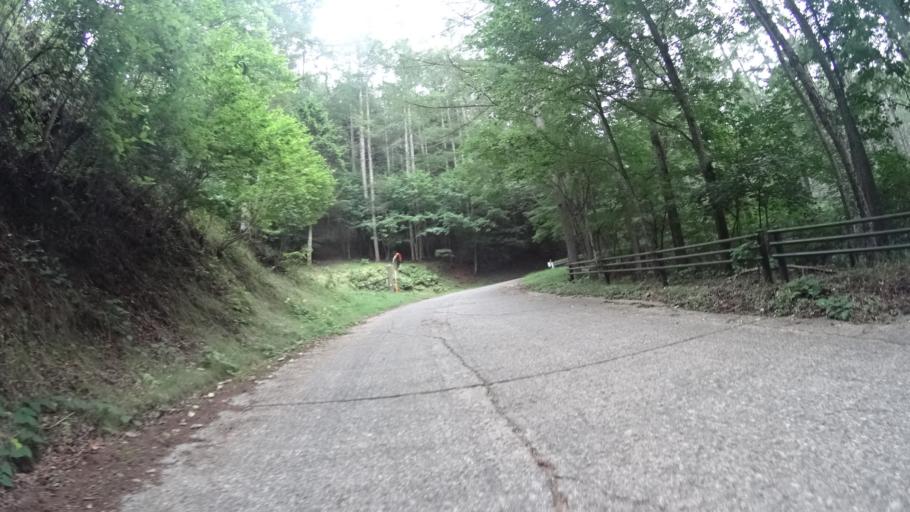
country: JP
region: Yamanashi
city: Kofu-shi
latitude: 35.8521
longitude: 138.5775
